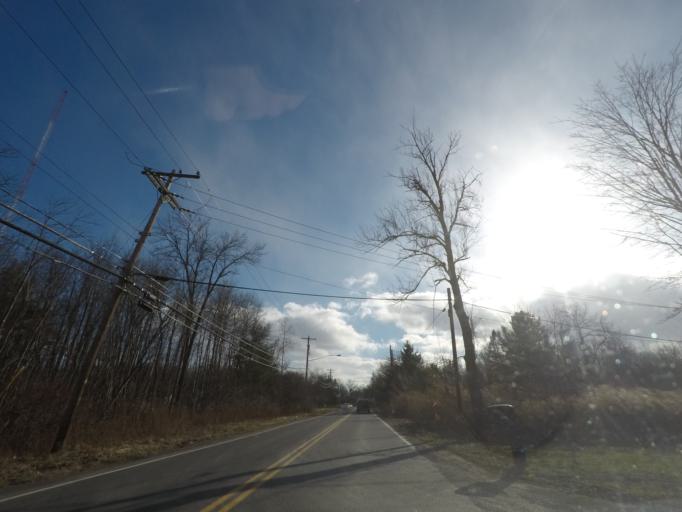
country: US
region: New York
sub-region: Albany County
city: Colonie
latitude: 42.7338
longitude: -73.8642
